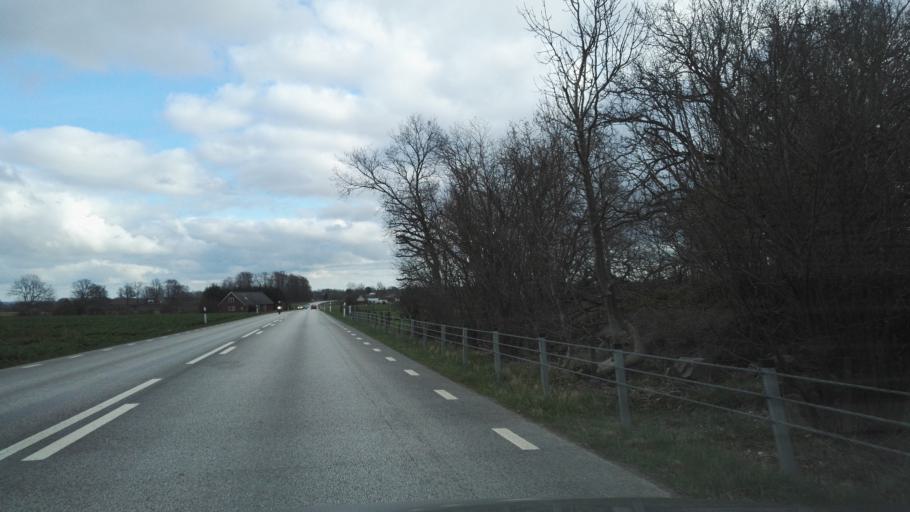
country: SE
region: Skane
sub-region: Sjobo Kommun
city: Sjoebo
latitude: 55.7267
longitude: 13.7130
